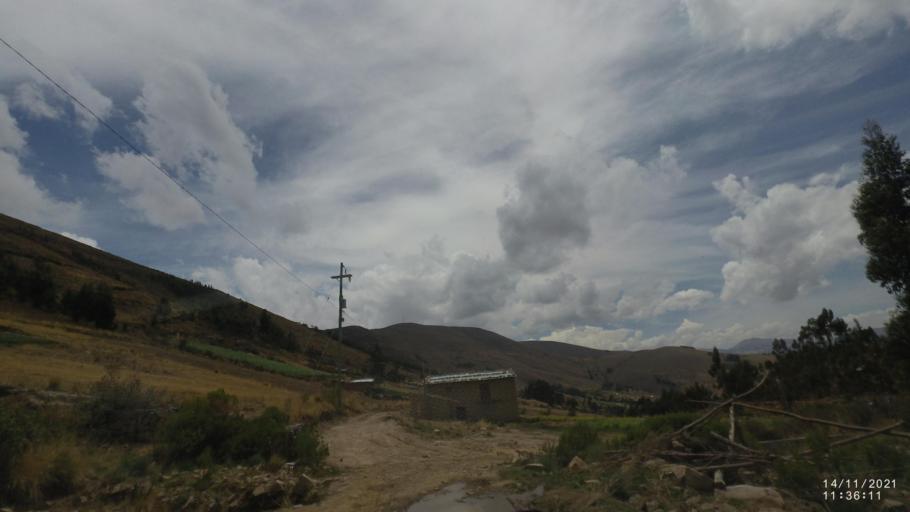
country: BO
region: Cochabamba
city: Colomi
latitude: -17.3462
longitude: -65.9990
